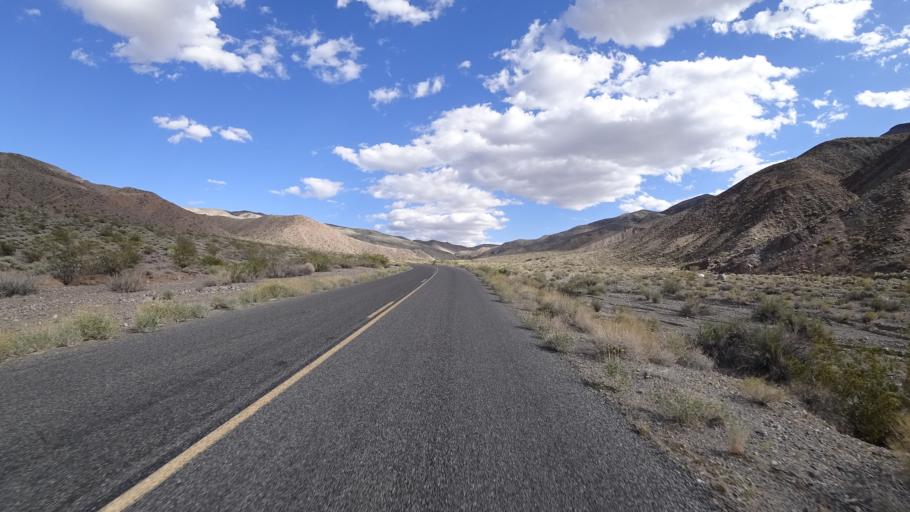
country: US
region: Nevada
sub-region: Nye County
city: Beatty
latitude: 36.4474
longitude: -117.1993
